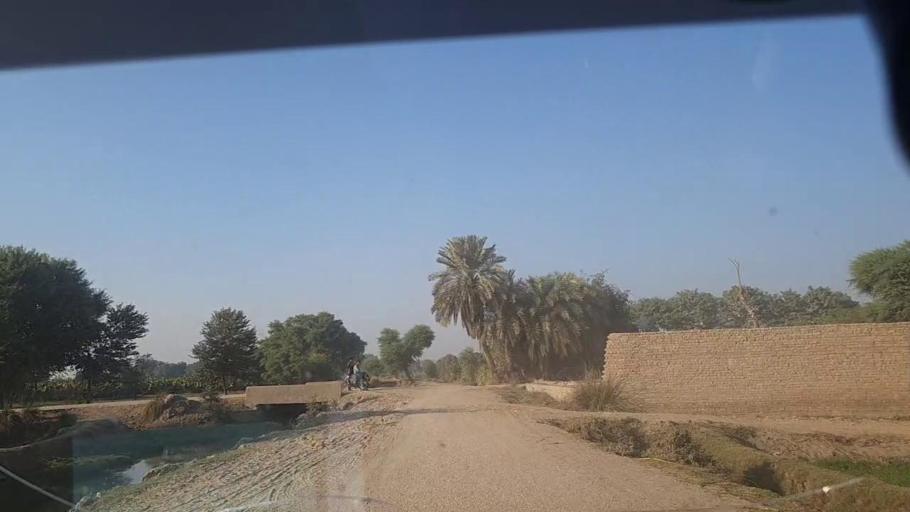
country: PK
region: Sindh
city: Sobhadero
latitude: 27.2695
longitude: 68.3476
